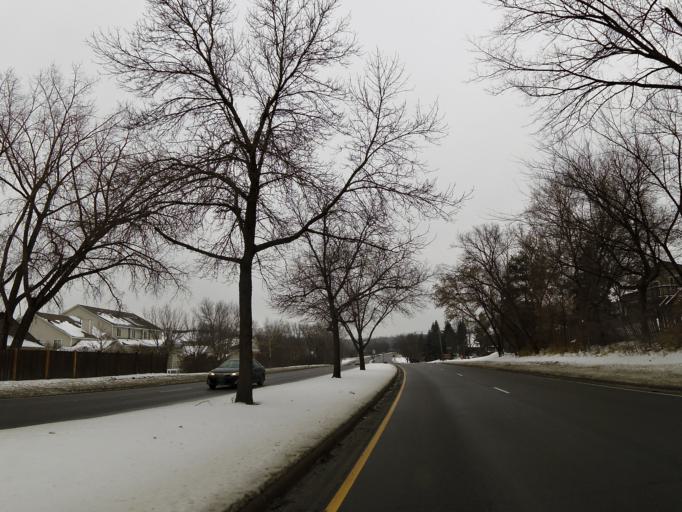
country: US
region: Minnesota
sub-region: Dakota County
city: Burnsville
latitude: 44.7633
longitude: -93.3040
